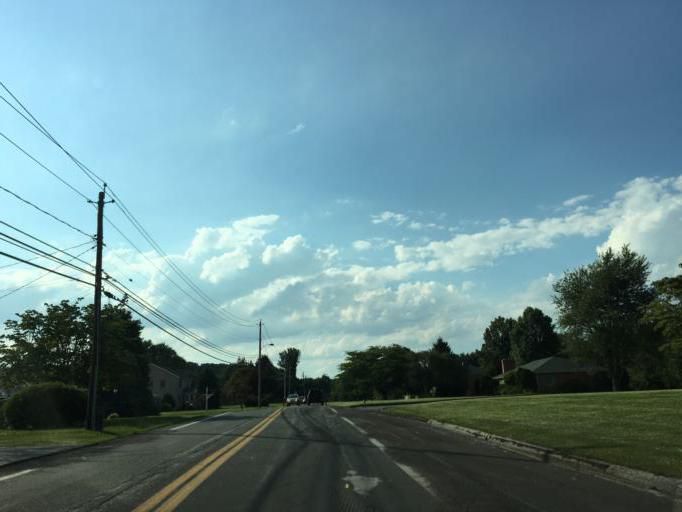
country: US
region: Maryland
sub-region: Baltimore County
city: Kingsville
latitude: 39.4374
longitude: -76.4349
